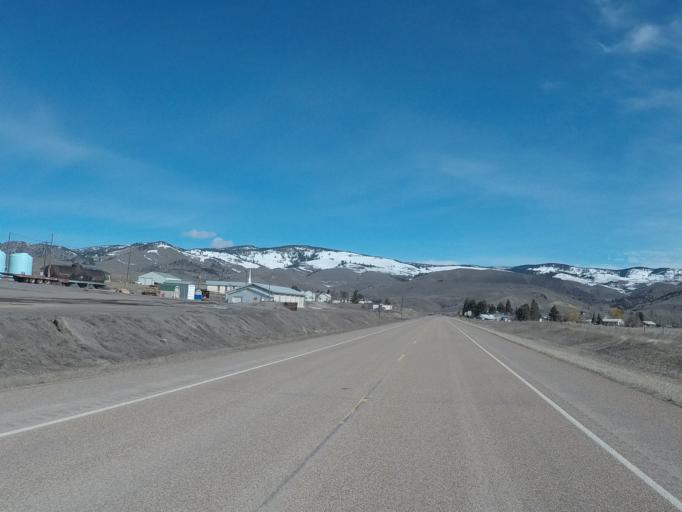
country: US
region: Montana
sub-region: Granite County
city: Philipsburg
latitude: 46.6556
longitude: -113.1597
